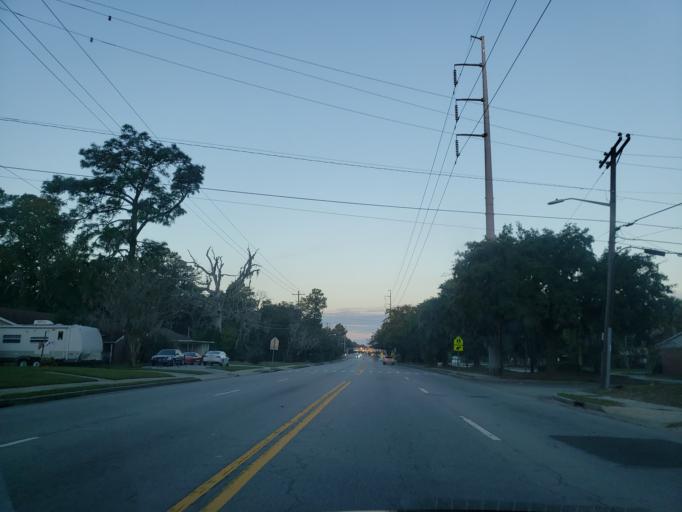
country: US
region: Georgia
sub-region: Chatham County
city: Thunderbolt
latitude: 32.0211
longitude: -81.0819
